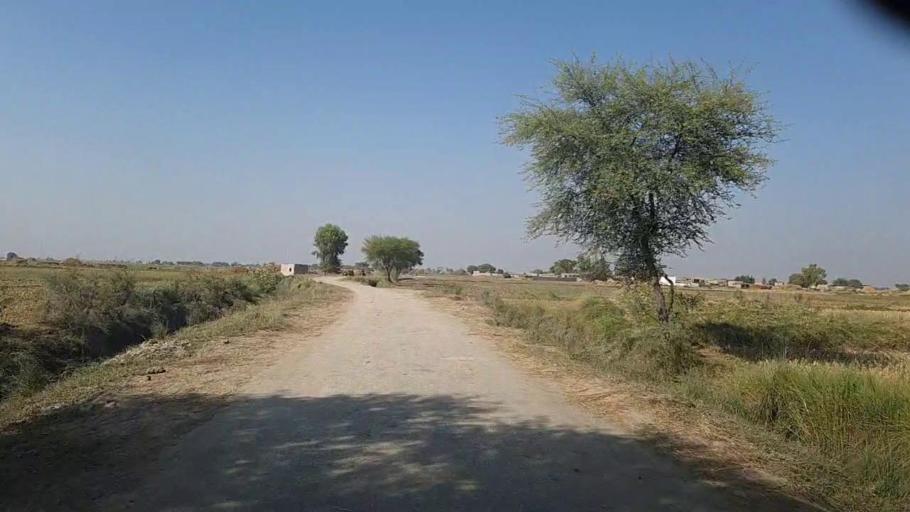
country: PK
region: Sindh
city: Tangwani
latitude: 28.2519
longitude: 68.9394
